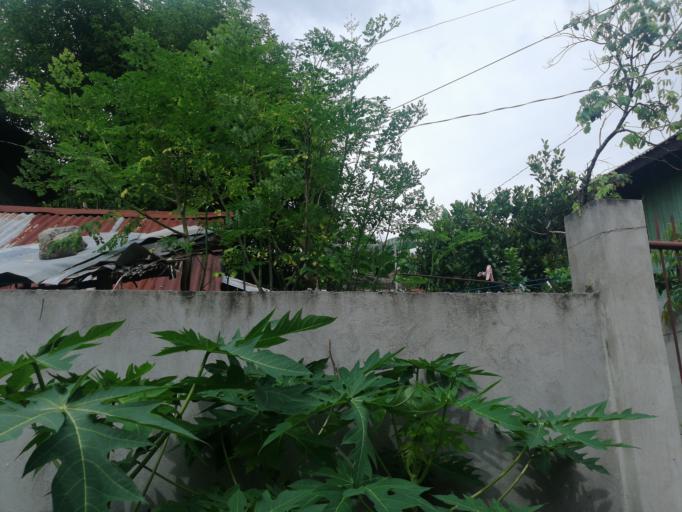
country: PH
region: Central Visayas
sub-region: Province of Negros Oriental
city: Dumaguete
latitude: 9.3029
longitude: 123.3000
